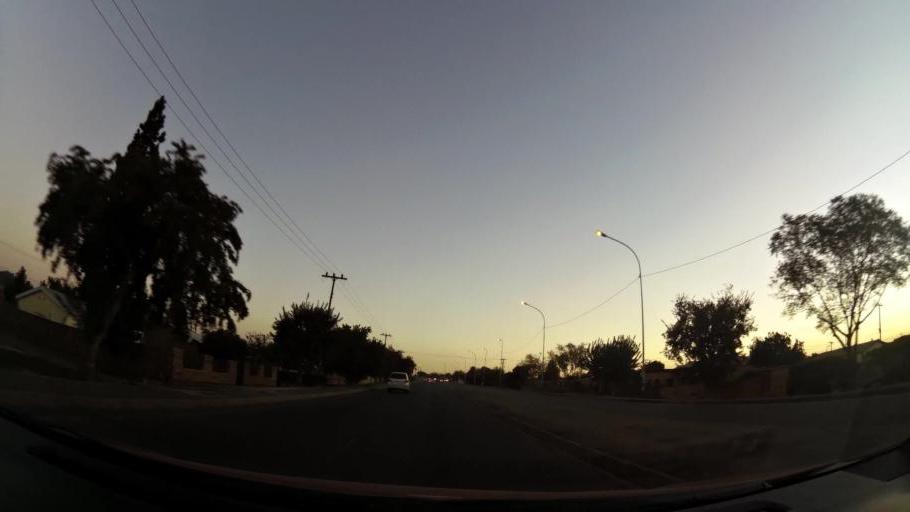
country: ZA
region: North-West
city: Ga-Rankuwa
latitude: -25.5983
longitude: 27.9760
